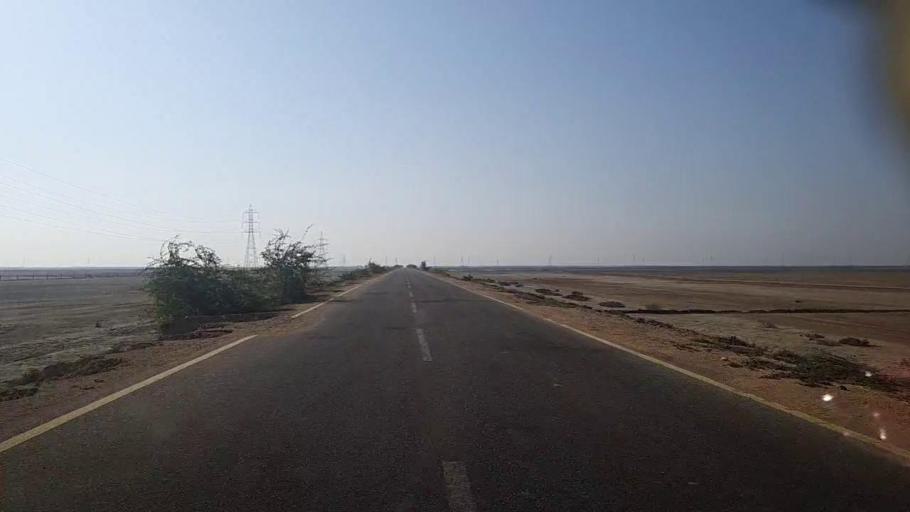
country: PK
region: Sindh
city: Mirpur Sakro
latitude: 24.6050
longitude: 67.4975
